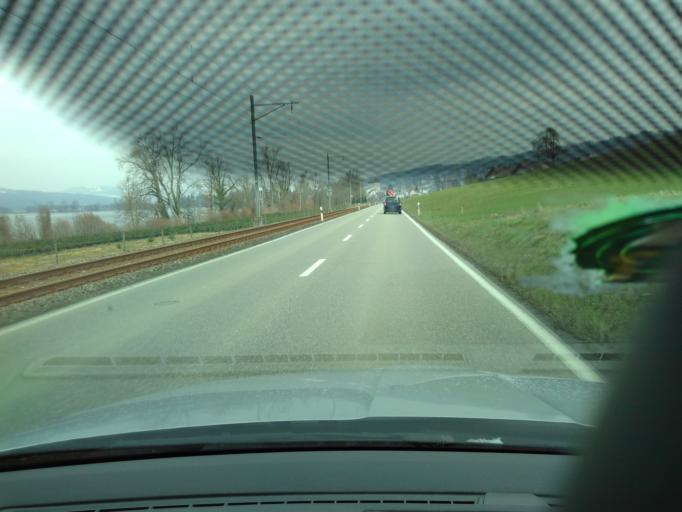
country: CH
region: Lucerne
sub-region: Hochdorf District
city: Hitzkirch
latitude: 47.2059
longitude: 8.2684
